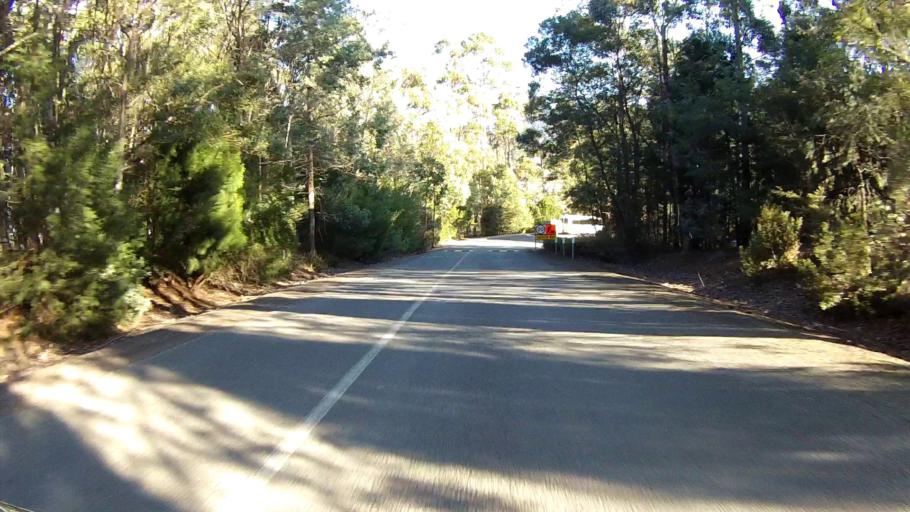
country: AU
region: Tasmania
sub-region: Clarence
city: Sandford
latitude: -43.1454
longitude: 147.8523
